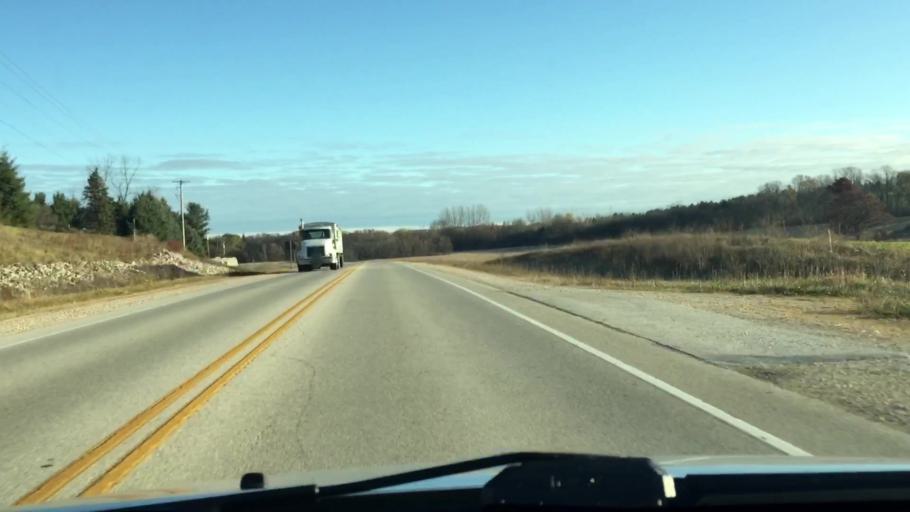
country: US
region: Wisconsin
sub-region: Dodge County
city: Theresa
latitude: 43.5379
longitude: -88.4453
